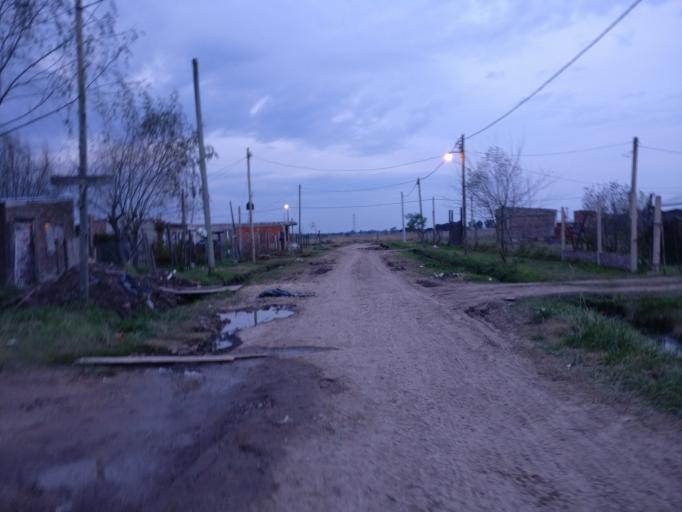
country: AR
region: Buenos Aires
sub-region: Partido de Ezeiza
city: Ezeiza
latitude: -34.9363
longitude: -58.6053
